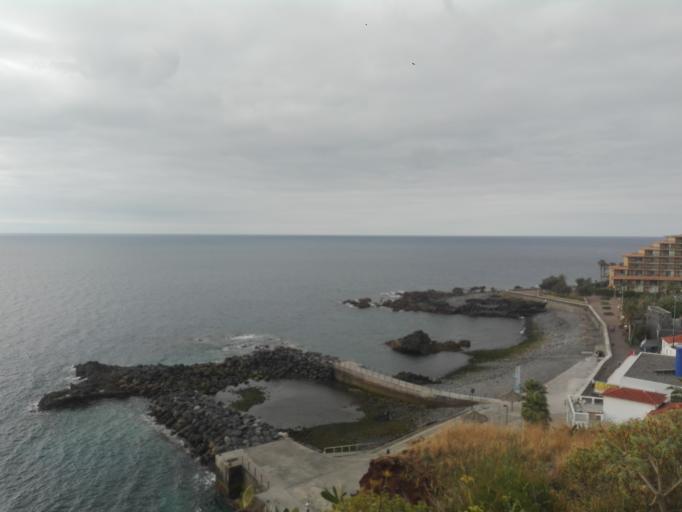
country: PT
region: Madeira
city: Canico
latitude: 32.6482
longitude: -16.8239
